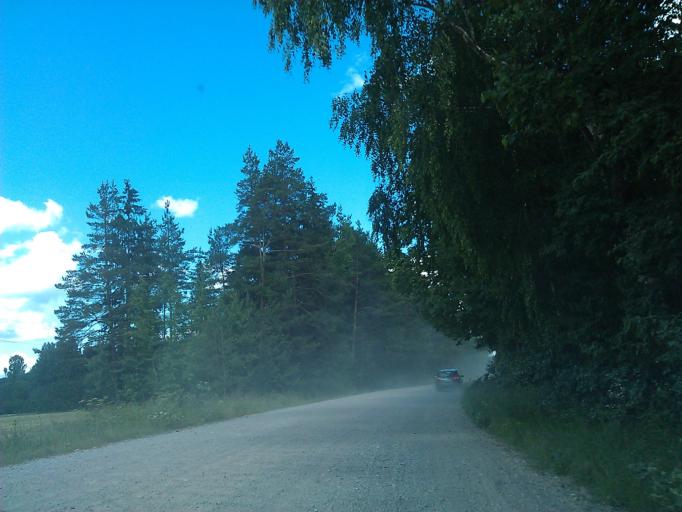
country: LV
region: Vilanu
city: Vilani
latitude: 56.5845
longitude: 26.9441
